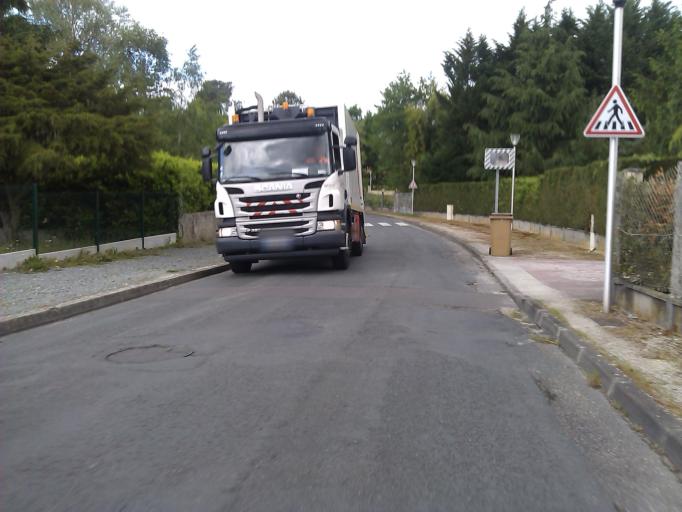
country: FR
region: Aquitaine
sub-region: Departement de la Gironde
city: Cestas
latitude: 44.7430
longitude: -0.6863
